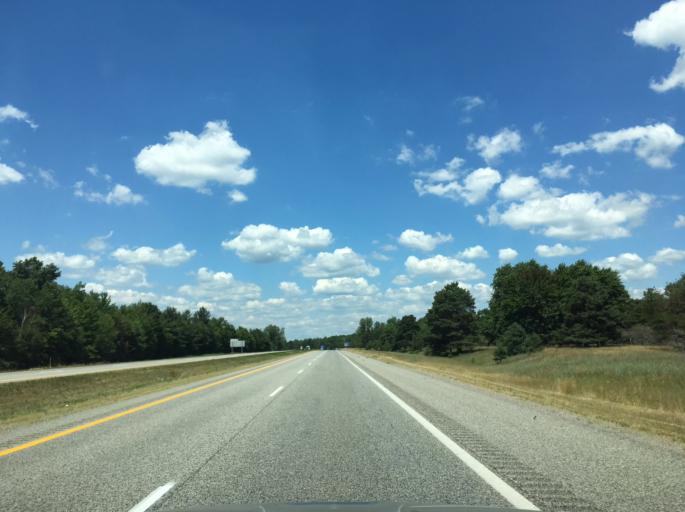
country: US
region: Michigan
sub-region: Midland County
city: Midland
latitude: 43.6515
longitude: -84.2018
